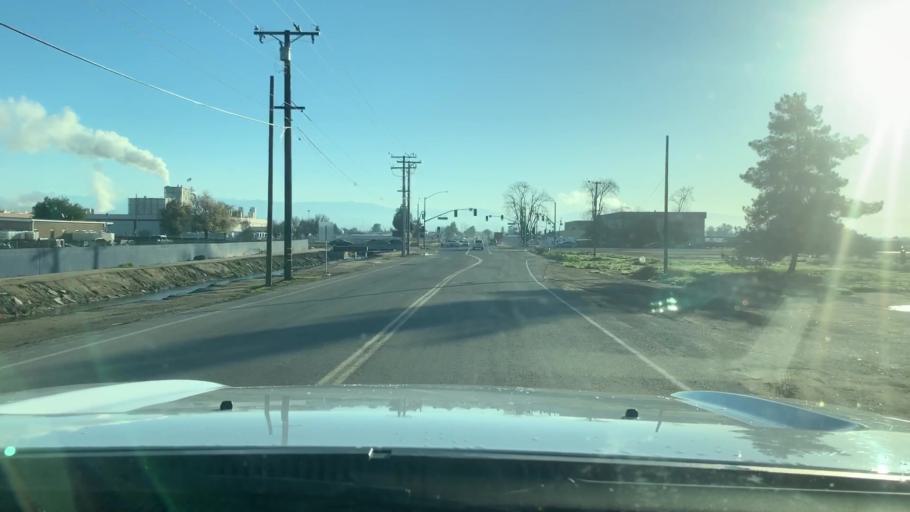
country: US
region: California
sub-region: Tulare County
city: Tulare
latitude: 36.1821
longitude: -119.3420
